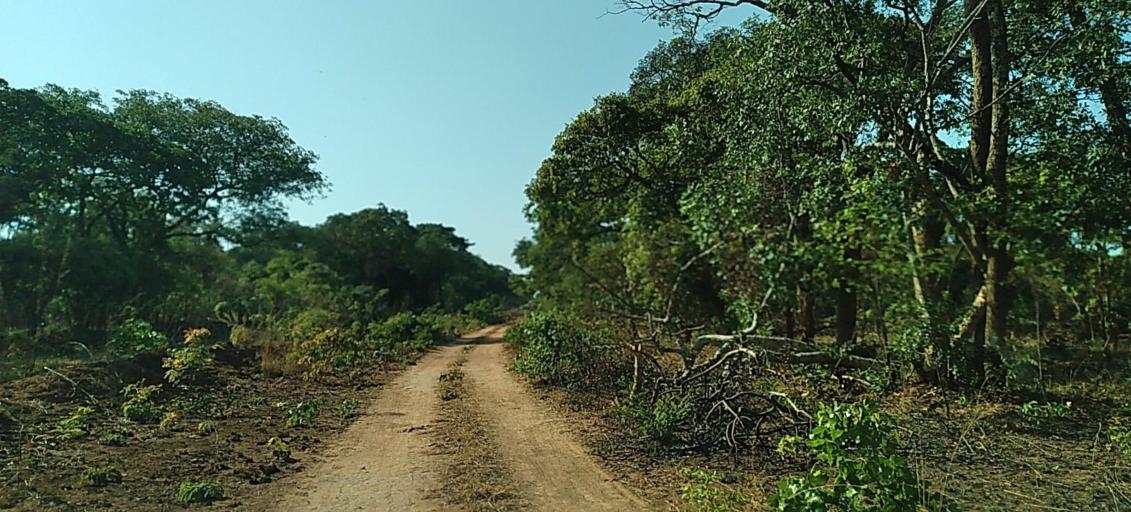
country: ZM
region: Central
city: Mkushi
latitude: -13.4579
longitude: 28.9102
